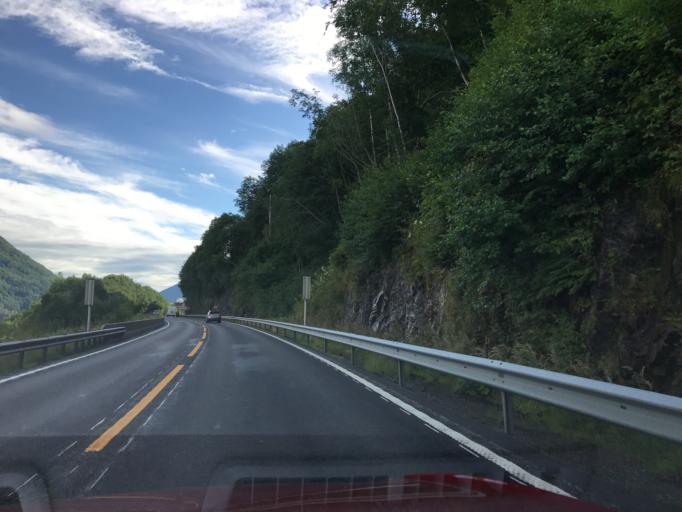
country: NO
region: Hordaland
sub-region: Bergen
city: Indre Arna
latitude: 60.4228
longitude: 5.5614
